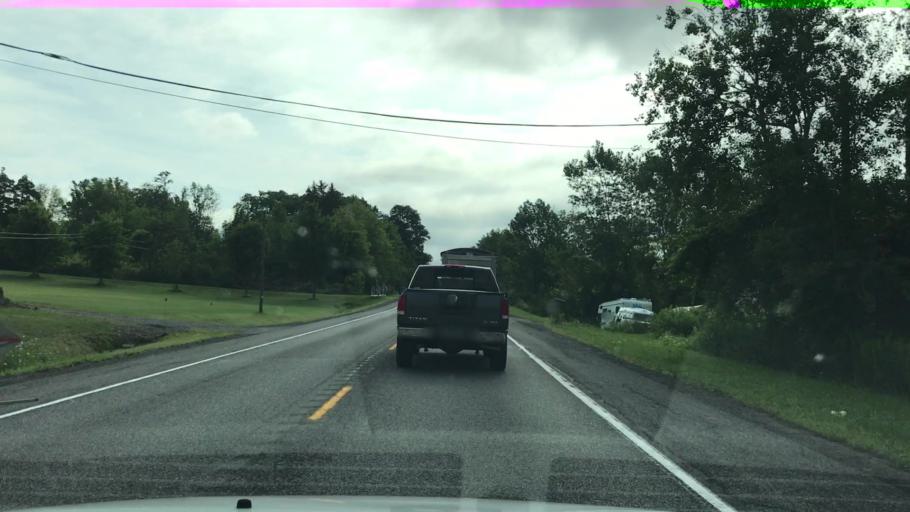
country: US
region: New York
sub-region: Erie County
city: Alden
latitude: 42.8353
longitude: -78.4195
